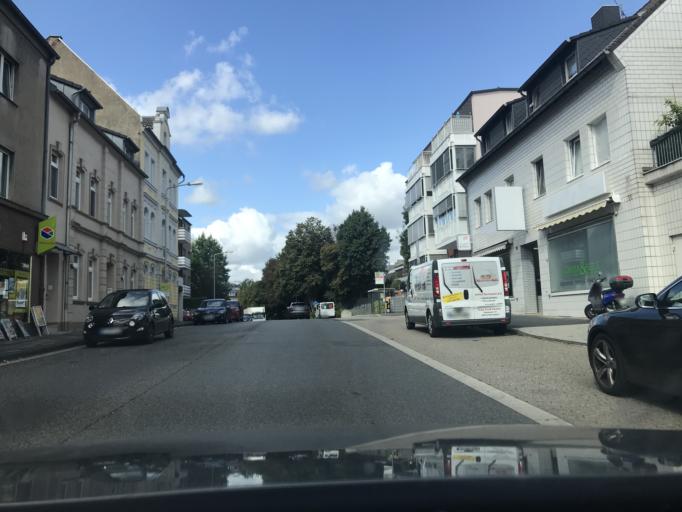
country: DE
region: North Rhine-Westphalia
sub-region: Regierungsbezirk Dusseldorf
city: Erkrath
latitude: 51.2259
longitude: 6.9039
